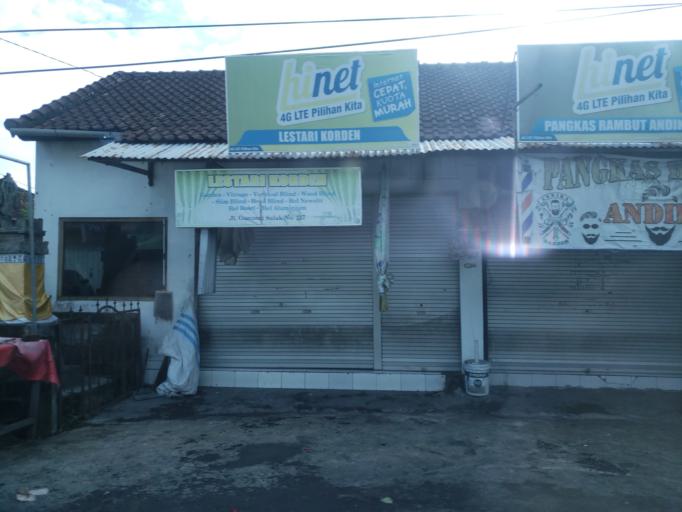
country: ID
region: Bali
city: Denpasar
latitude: -8.6776
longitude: 115.1807
